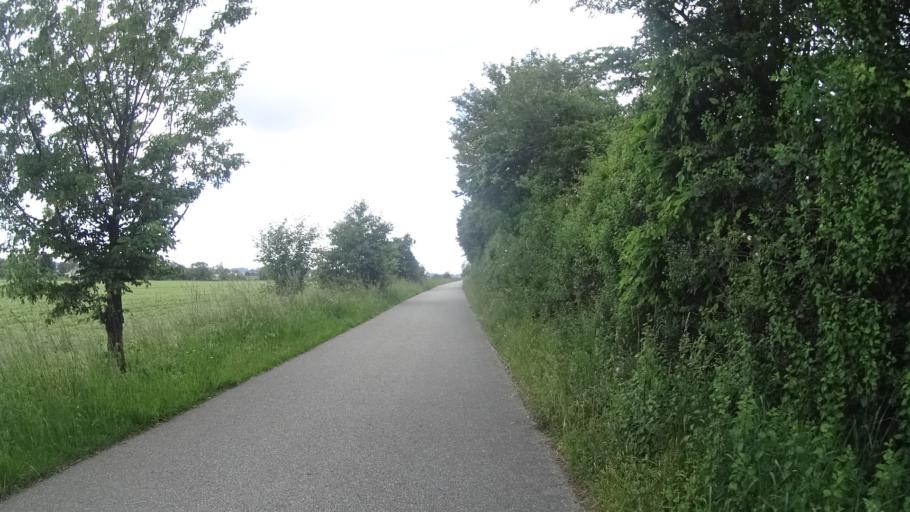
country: DE
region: Bavaria
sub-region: Lower Bavaria
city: Eggenfelden
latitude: 48.3969
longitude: 12.7435
